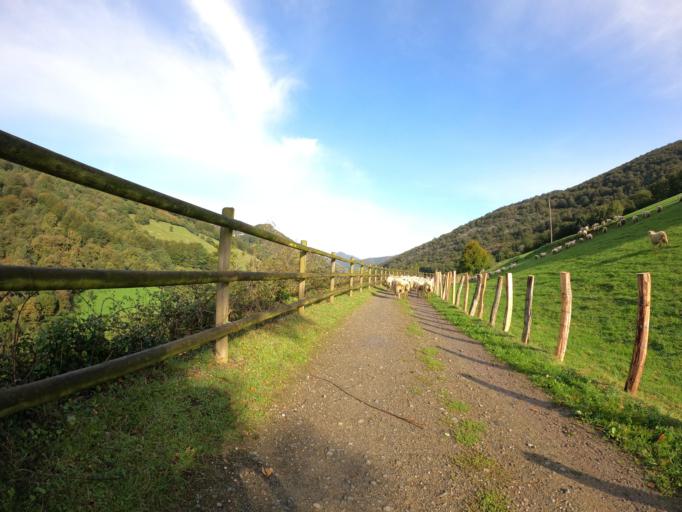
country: ES
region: Navarre
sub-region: Provincia de Navarra
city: Leitza
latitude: 43.0596
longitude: -1.9085
